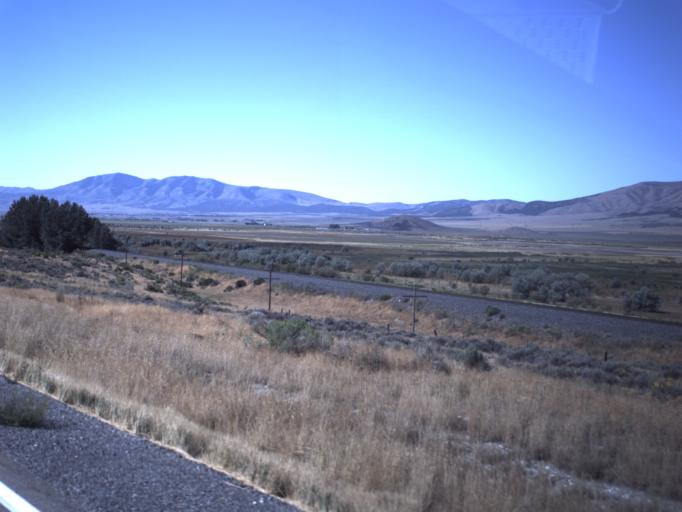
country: US
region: Utah
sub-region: Tooele County
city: Tooele
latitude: 40.4257
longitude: -112.3806
